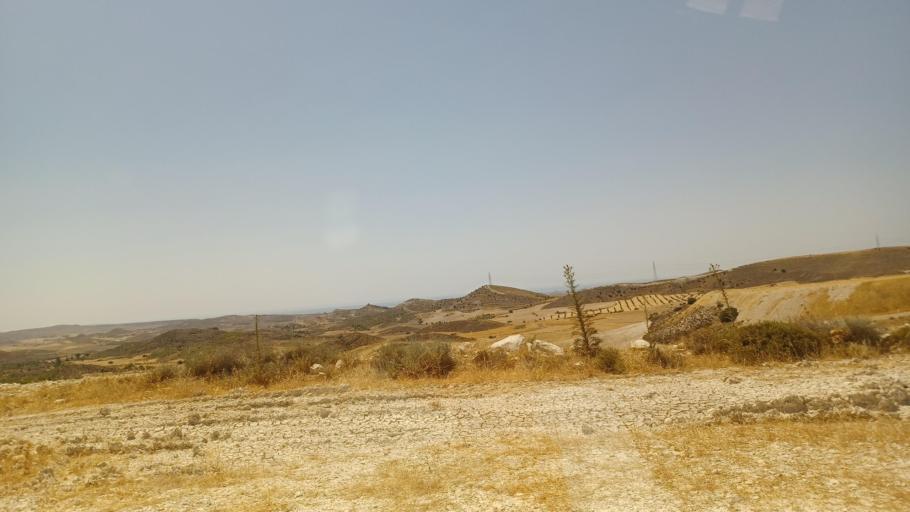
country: CY
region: Larnaka
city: Athienou
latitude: 35.0049
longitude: 33.5536
